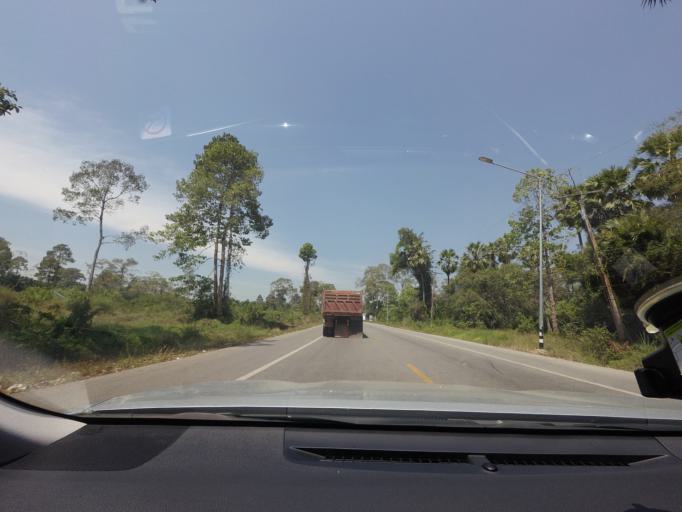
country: TH
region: Surat Thani
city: Tha Chang
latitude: 9.2603
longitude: 99.1834
